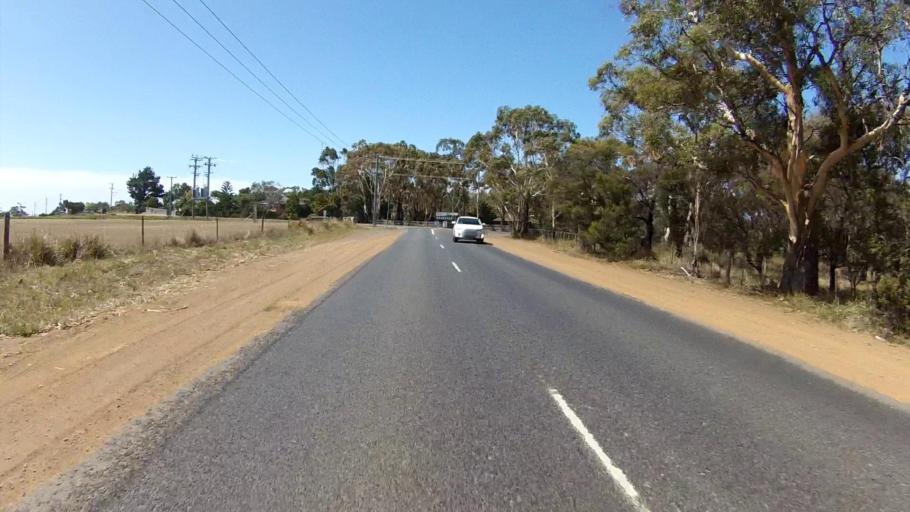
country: AU
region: Tasmania
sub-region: Clarence
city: Sandford
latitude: -42.9361
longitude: 147.4918
